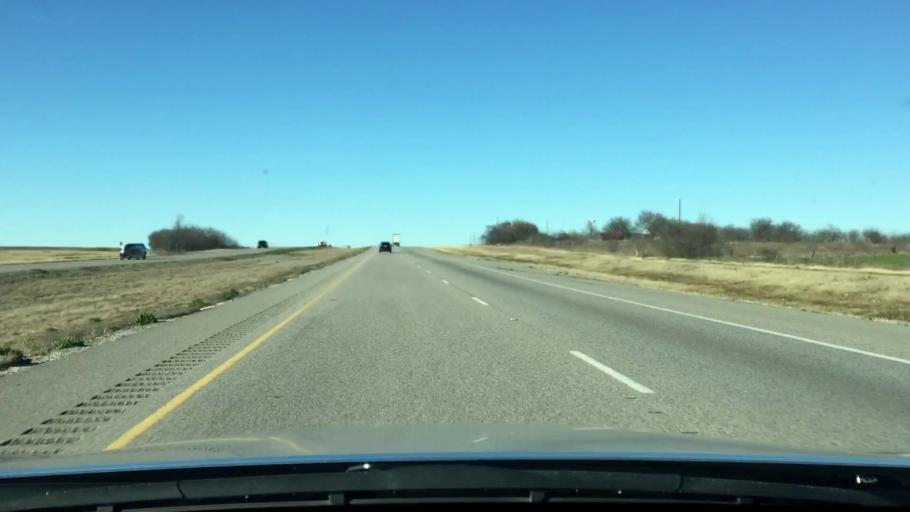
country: US
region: Texas
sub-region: Hill County
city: Itasca
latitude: 32.1165
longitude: -97.1148
